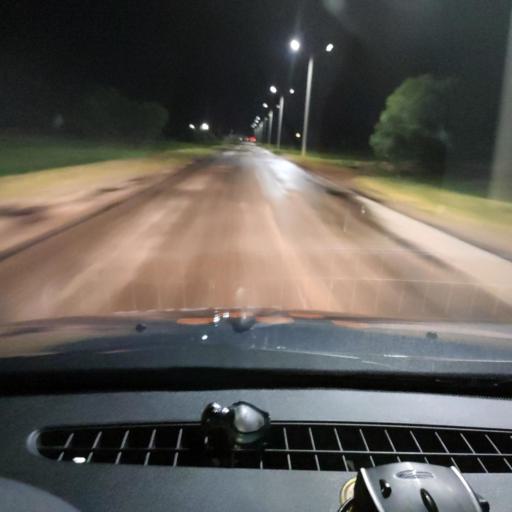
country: RU
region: Voronezj
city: Khrenovoye
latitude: 51.1235
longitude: 40.2739
